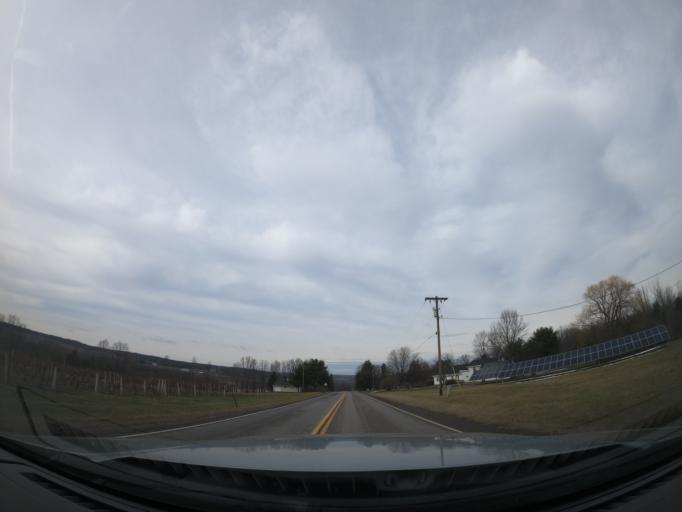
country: US
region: New York
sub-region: Yates County
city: Dundee
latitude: 42.5016
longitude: -76.9541
